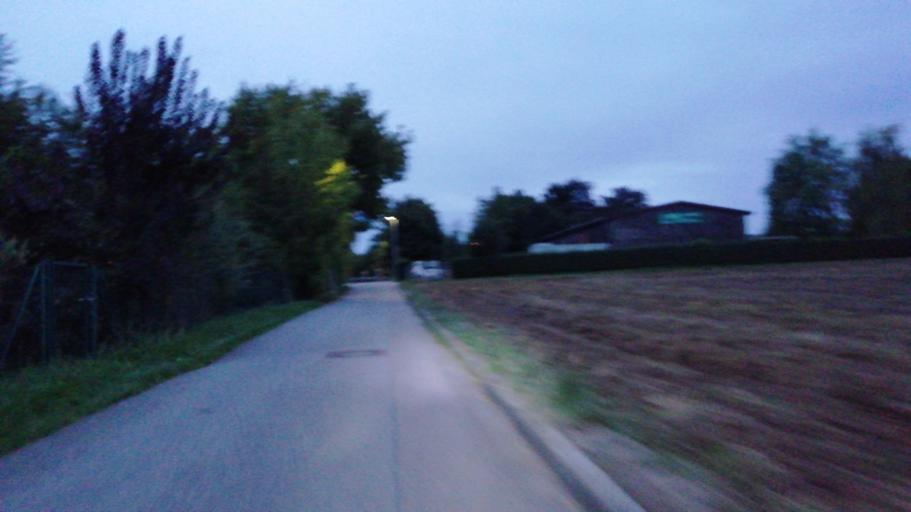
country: DE
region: Baden-Wuerttemberg
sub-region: Regierungsbezirk Stuttgart
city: Korntal
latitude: 48.8114
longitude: 9.1078
